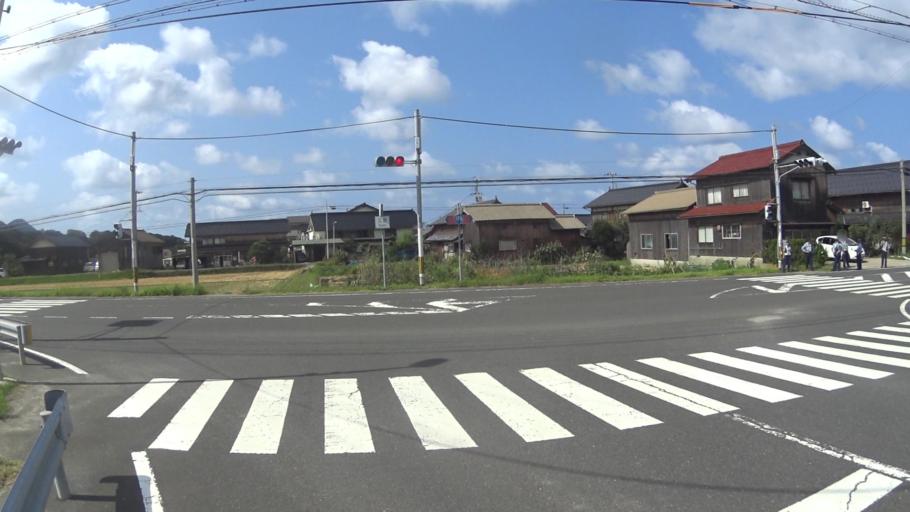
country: JP
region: Kyoto
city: Miyazu
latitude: 35.7557
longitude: 135.1737
